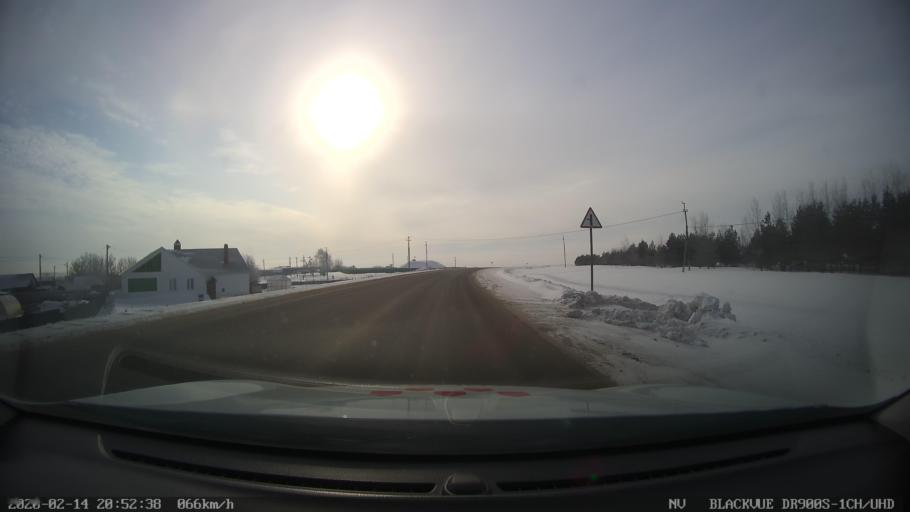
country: RU
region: Tatarstan
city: Kuybyshevskiy Zaton
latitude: 55.2022
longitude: 49.2498
